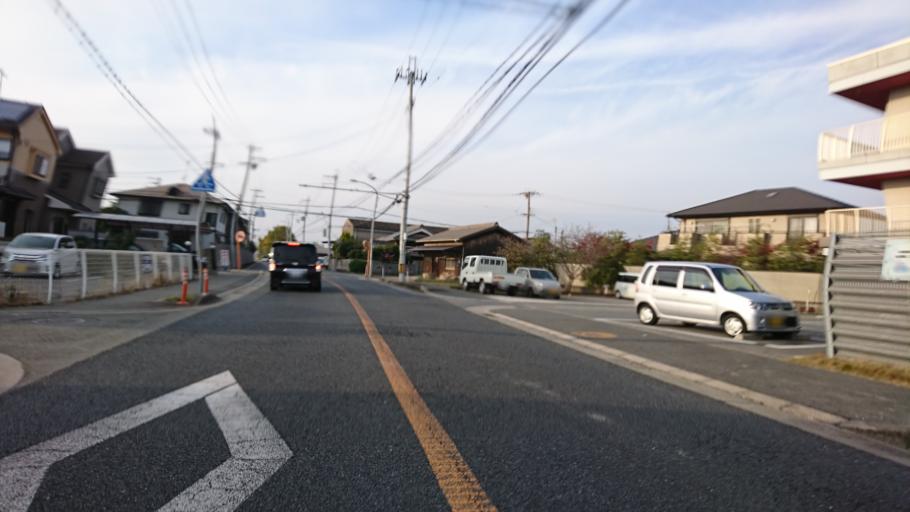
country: JP
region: Hyogo
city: Kakogawacho-honmachi
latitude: 34.7292
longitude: 134.8396
